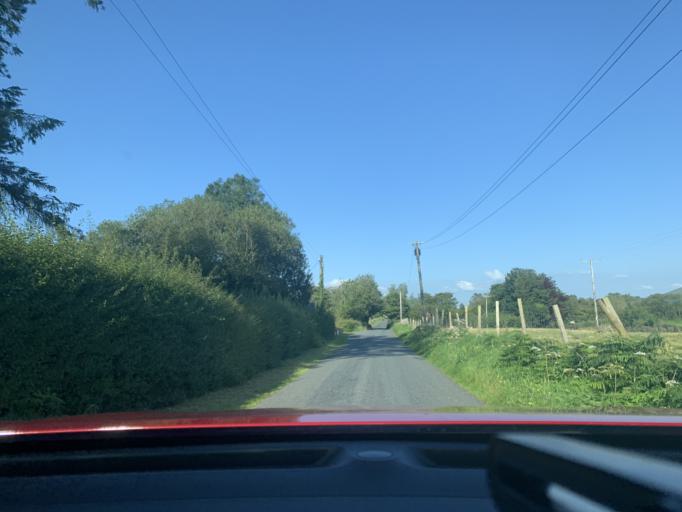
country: IE
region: Connaught
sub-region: Sligo
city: Tobercurry
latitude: 54.1211
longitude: -8.7498
